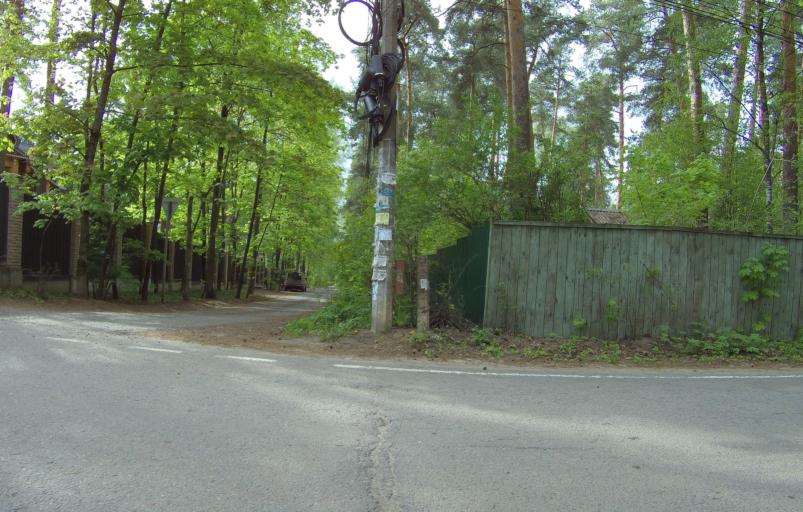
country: RU
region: Moskovskaya
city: Kratovo
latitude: 55.5786
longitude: 38.1795
